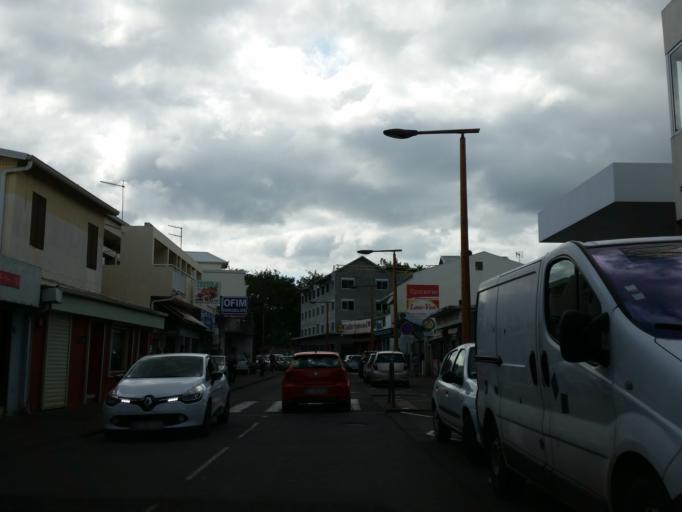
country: RE
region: Reunion
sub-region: Reunion
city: Sainte-Marie
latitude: -20.8970
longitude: 55.5502
